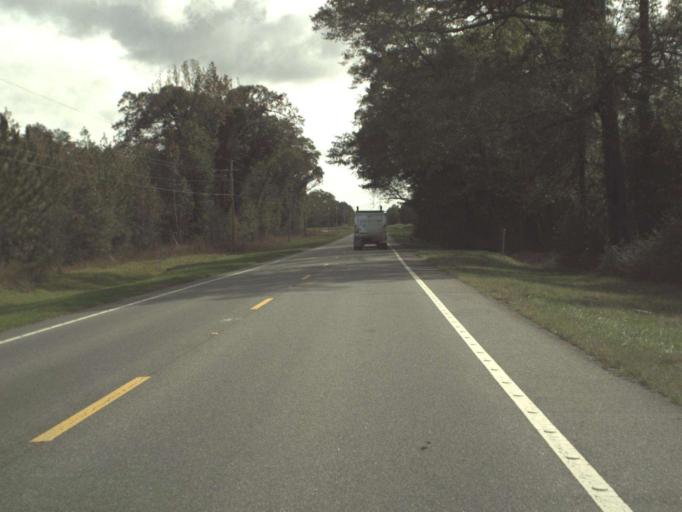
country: US
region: Alabama
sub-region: Escambia County
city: East Brewton
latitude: 30.9447
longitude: -87.0320
